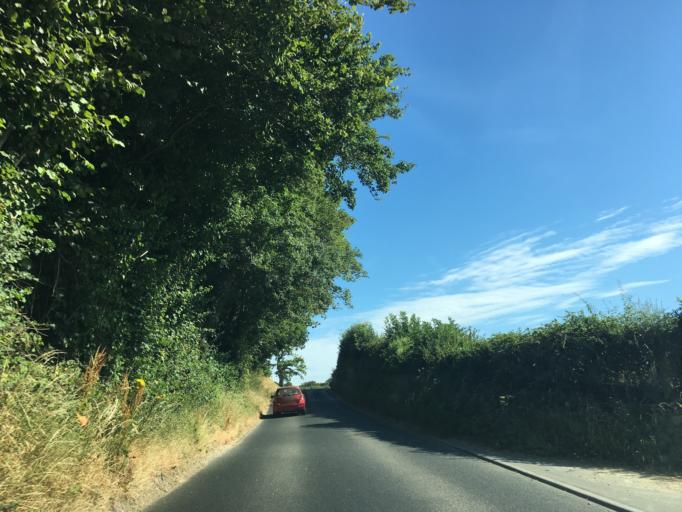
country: GB
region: England
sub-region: Isle of Wight
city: Newport
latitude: 50.6836
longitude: -1.3115
